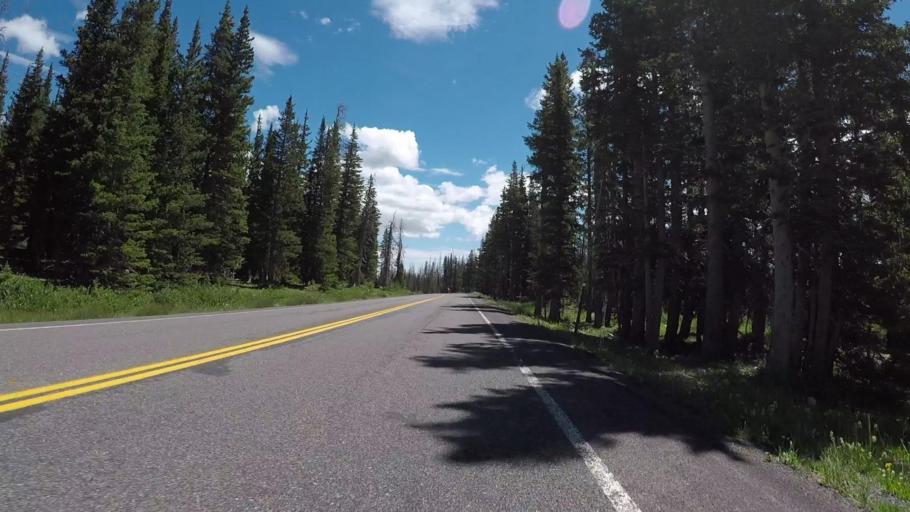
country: US
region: Wyoming
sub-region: Carbon County
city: Saratoga
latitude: 41.3505
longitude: -106.2554
